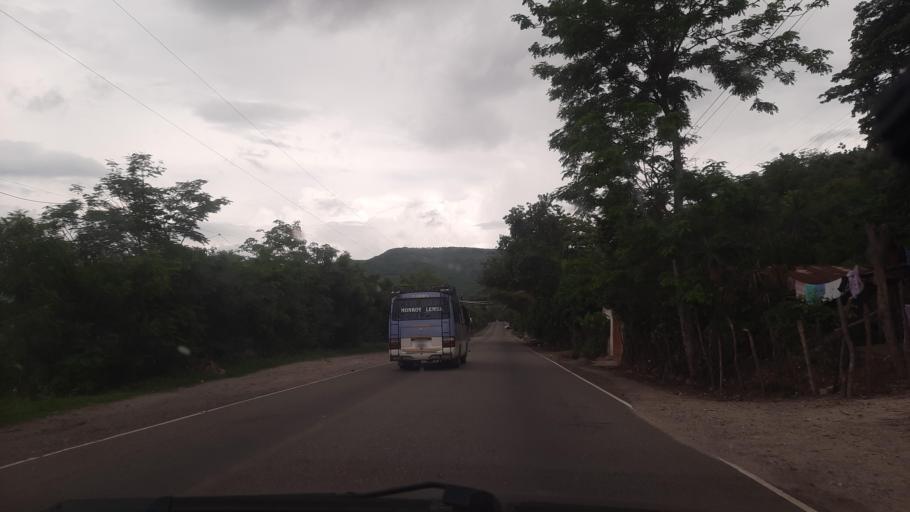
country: GT
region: Zacapa
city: Zacapa
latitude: 14.9157
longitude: -89.5296
